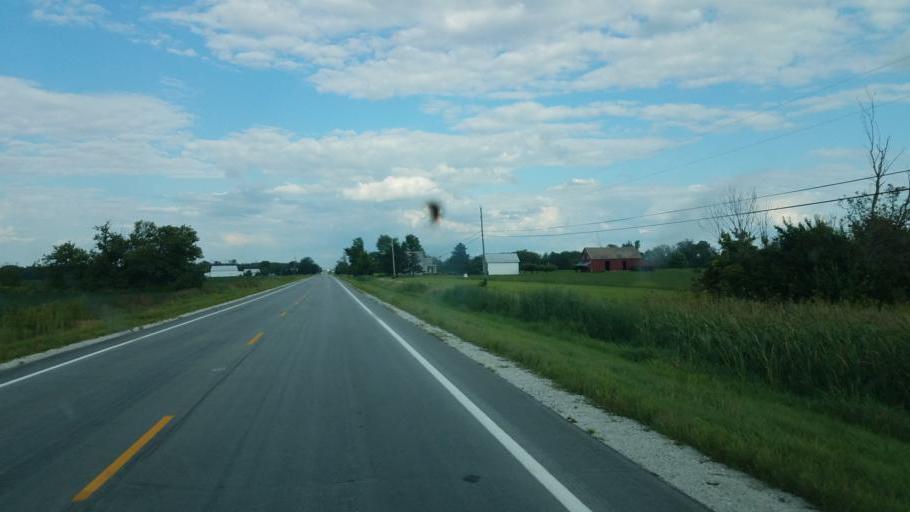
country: US
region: Ohio
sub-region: Sandusky County
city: Gibsonburg
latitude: 41.3413
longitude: -83.2636
